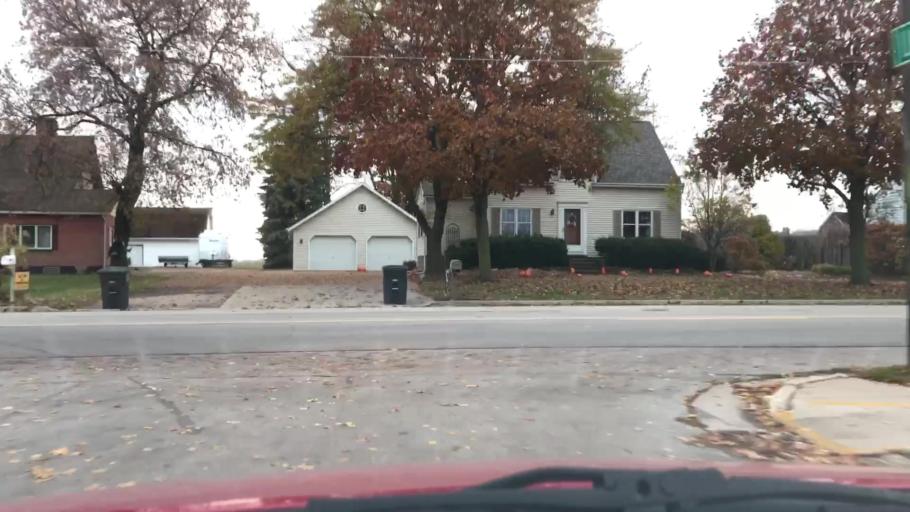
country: US
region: Wisconsin
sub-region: Outagamie County
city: Seymour
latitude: 44.5008
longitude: -88.3320
